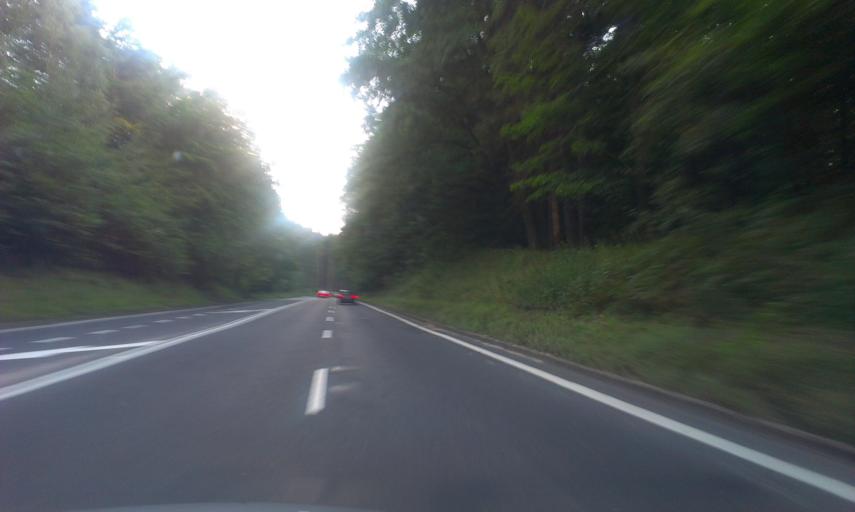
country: PL
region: West Pomeranian Voivodeship
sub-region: Koszalin
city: Koszalin
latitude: 54.2158
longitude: 16.2229
